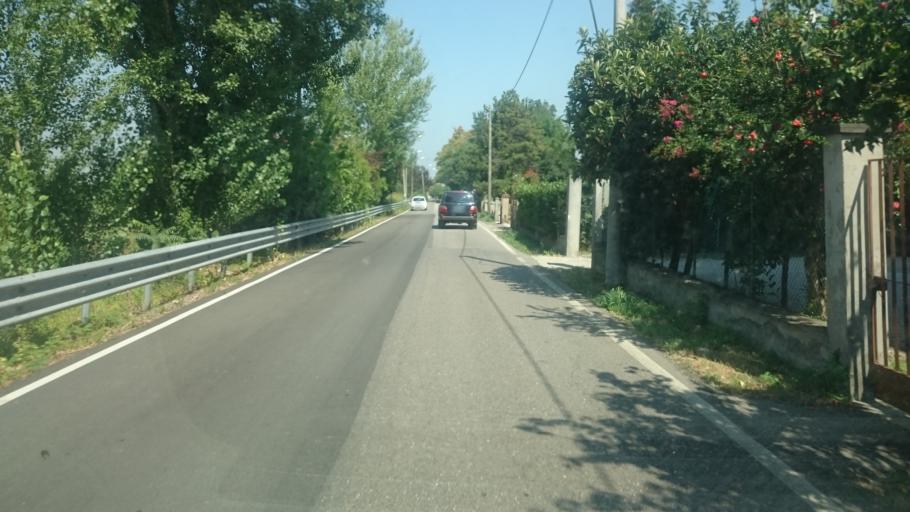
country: IT
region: Emilia-Romagna
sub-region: Provincia di Reggio Emilia
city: Fellegara
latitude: 44.6335
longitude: 10.6810
